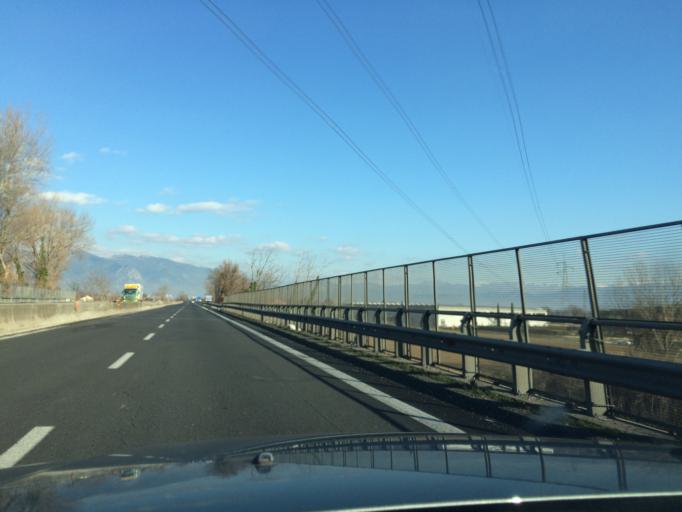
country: IT
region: Umbria
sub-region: Provincia di Terni
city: Narni Scalo
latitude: 42.5499
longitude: 12.5259
